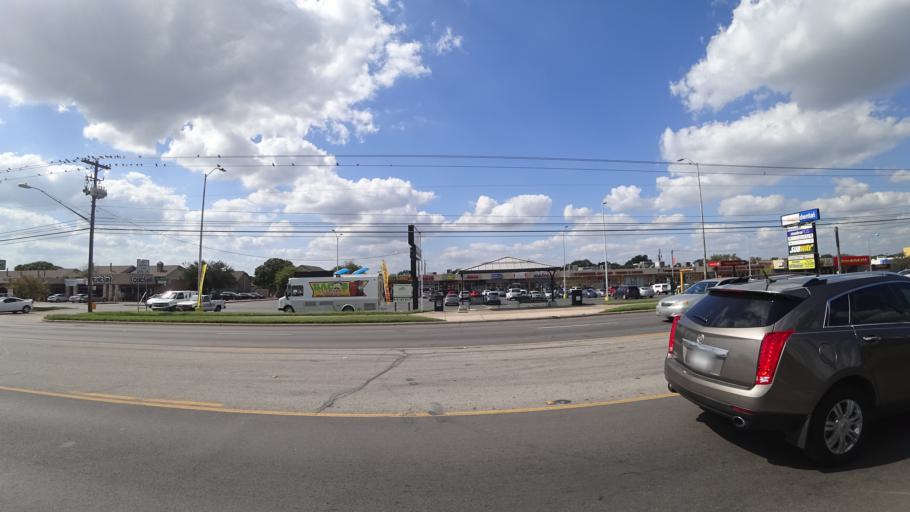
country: US
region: Texas
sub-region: Travis County
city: Wells Branch
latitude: 30.3617
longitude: -97.6977
